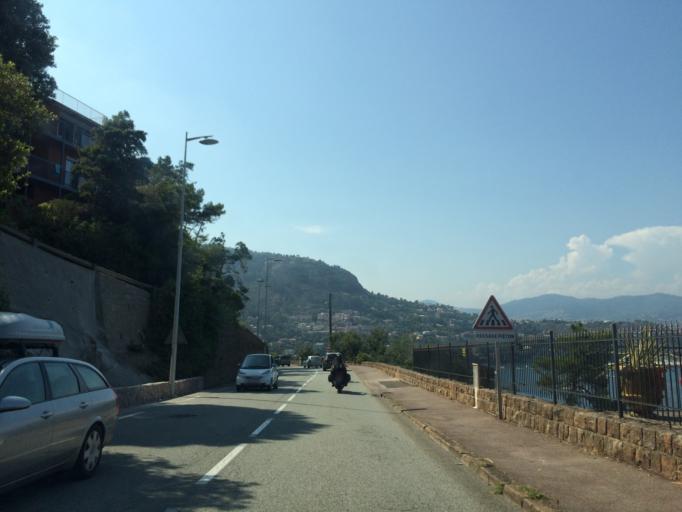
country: FR
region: Provence-Alpes-Cote d'Azur
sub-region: Departement des Alpes-Maritimes
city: Theoule-sur-Mer
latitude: 43.5055
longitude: 6.9458
